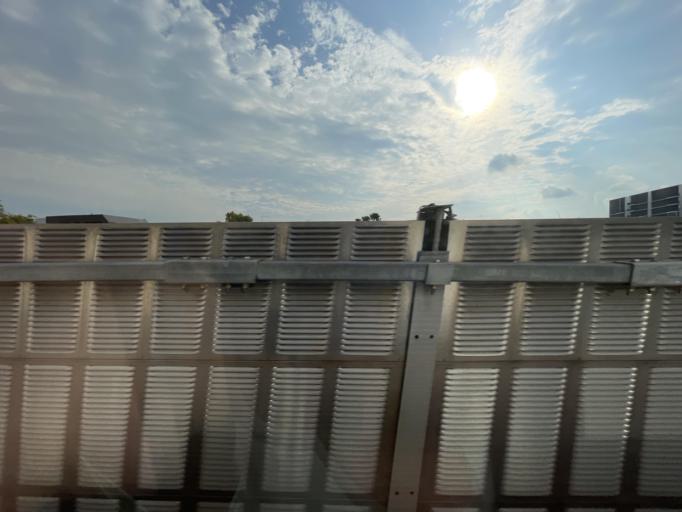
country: SG
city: Singapore
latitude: 1.3407
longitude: 103.9553
